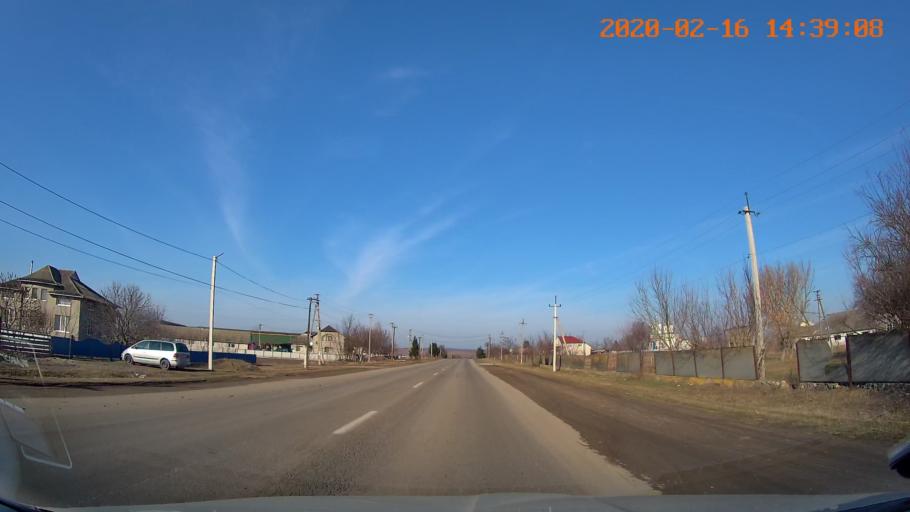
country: RO
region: Botosani
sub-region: Comuna Darabani
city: Bajura
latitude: 48.2390
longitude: 26.5474
